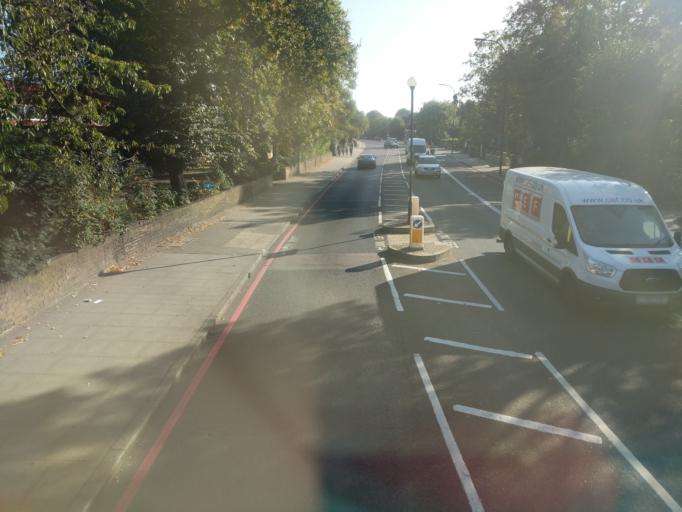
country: GB
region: England
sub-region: Greater London
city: Catford
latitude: 51.4427
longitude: -0.0202
